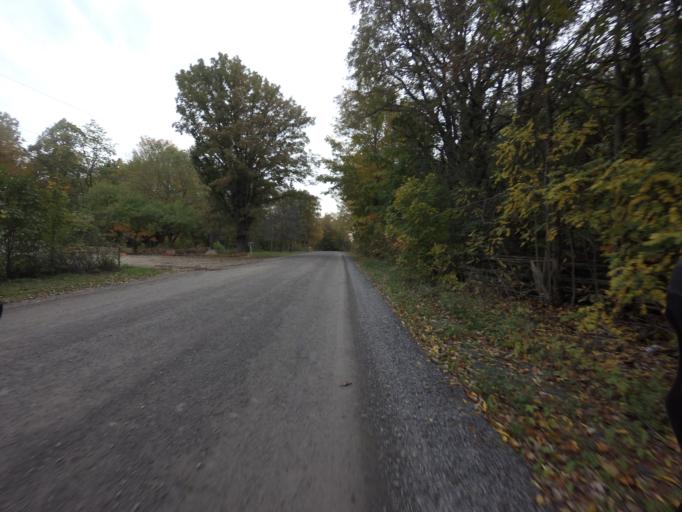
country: CA
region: Ontario
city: Bells Corners
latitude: 45.0712
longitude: -75.7570
